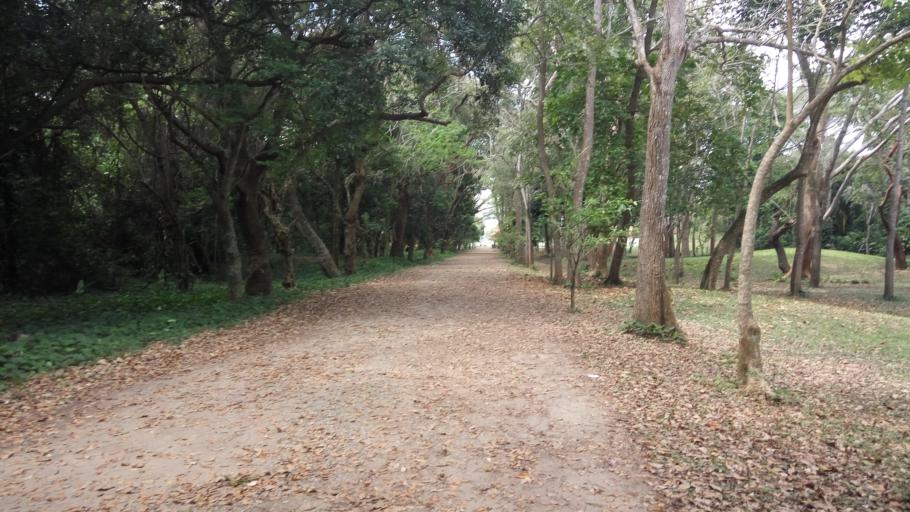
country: MX
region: Tabasco
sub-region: Comalcalco
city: Oriente 1ra. Seccion (Santo Domingo)
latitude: 18.2798
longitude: -93.2029
